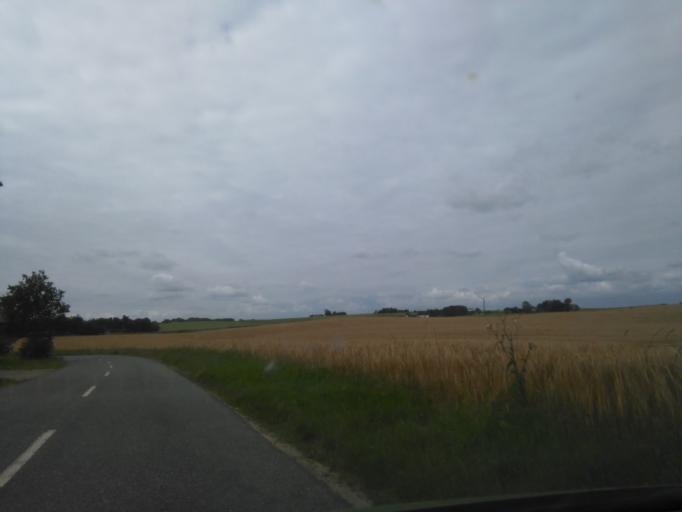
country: DK
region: Central Jutland
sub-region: Arhus Kommune
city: Solbjerg
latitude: 56.0190
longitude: 10.0730
